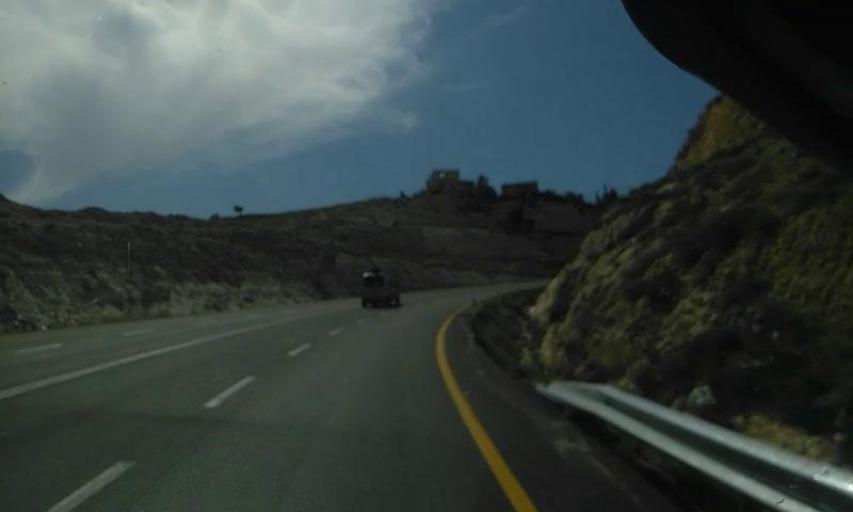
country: PS
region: West Bank
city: Bayt Ta`mar
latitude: 31.6734
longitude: 35.2435
